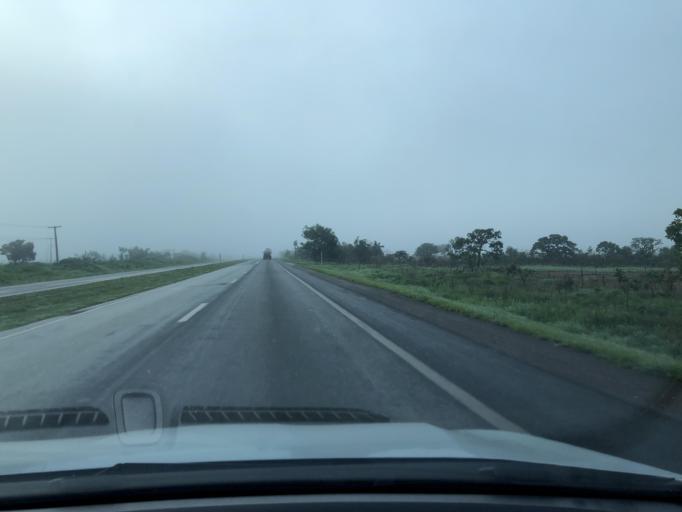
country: BR
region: Goias
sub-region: Luziania
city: Luziania
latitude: -16.2965
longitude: -47.8493
